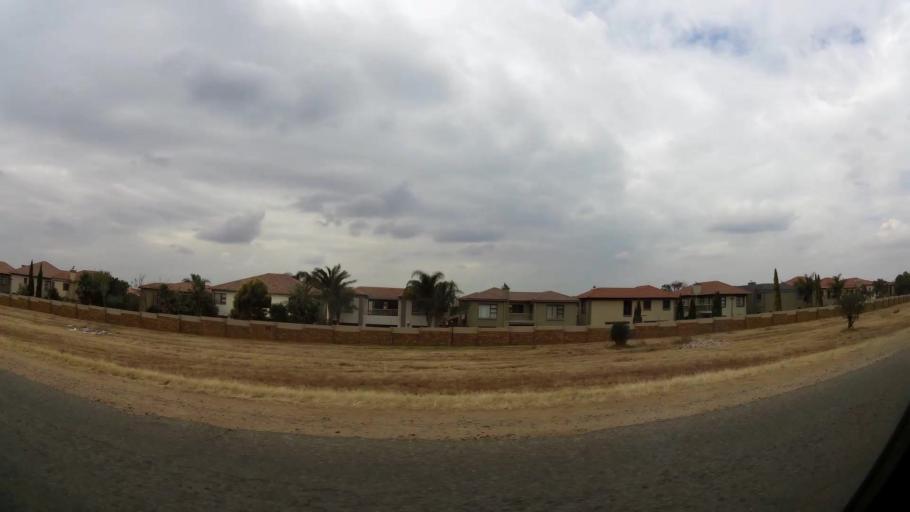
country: ZA
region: Gauteng
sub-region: City of Johannesburg Metropolitan Municipality
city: Roodepoort
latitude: -26.0967
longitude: 27.8743
